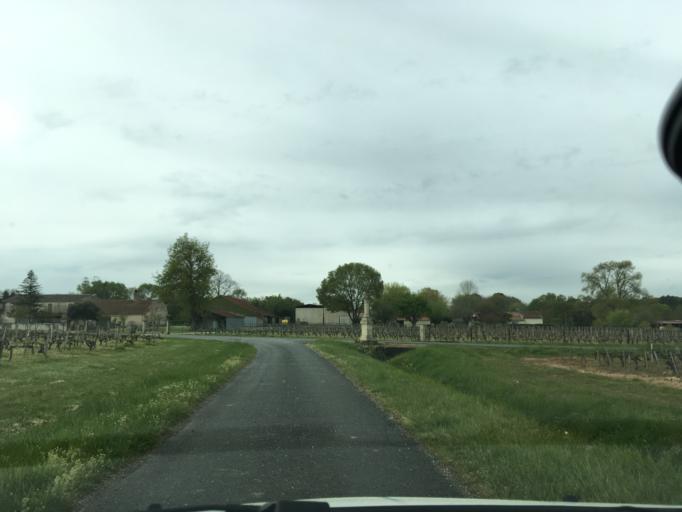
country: FR
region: Aquitaine
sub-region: Departement de la Gironde
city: Lesparre-Medoc
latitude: 45.3149
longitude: -0.8949
